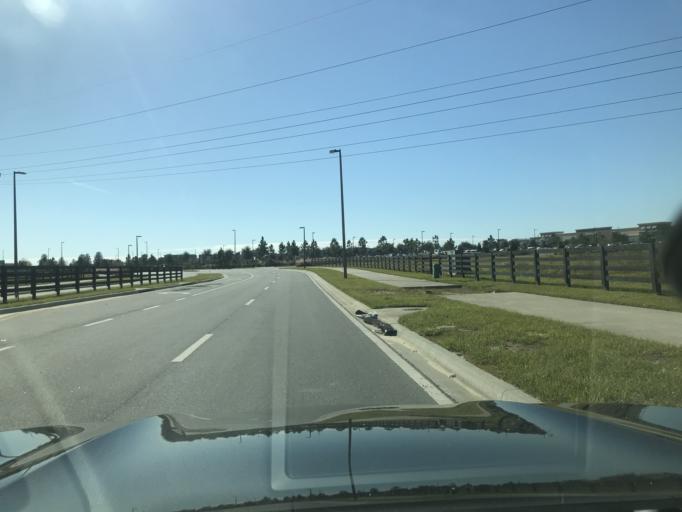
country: US
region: Florida
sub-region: Orange County
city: Oakland
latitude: 28.4796
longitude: -81.6275
